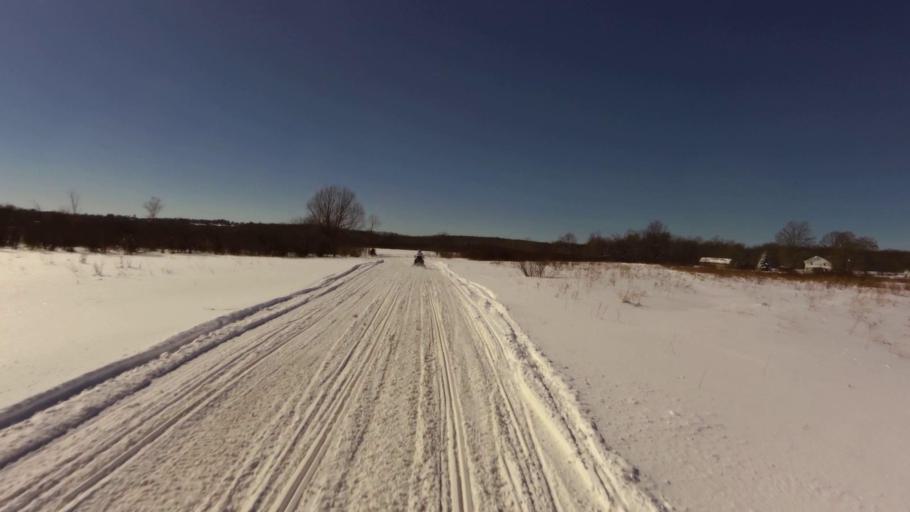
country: US
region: New York
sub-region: Chautauqua County
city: Mayville
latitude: 42.2721
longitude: -79.4863
